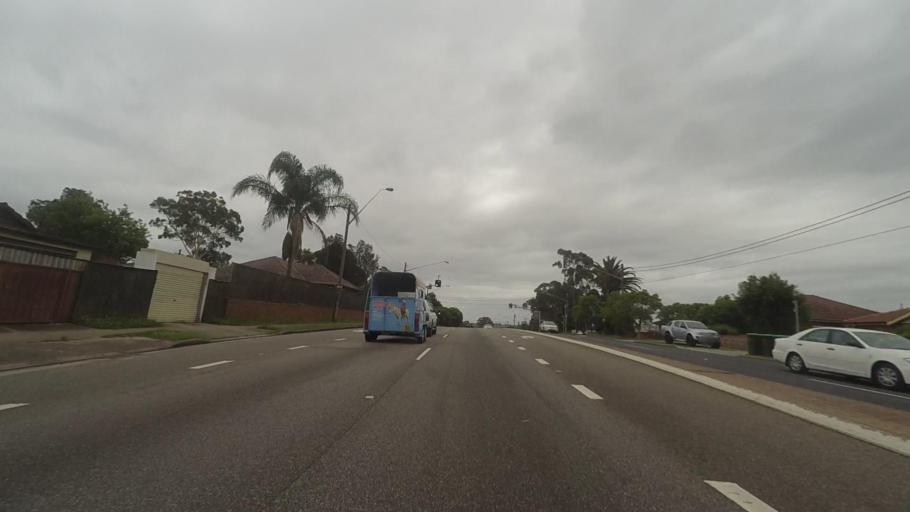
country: AU
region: New South Wales
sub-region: Bankstown
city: Padstow
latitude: -33.9546
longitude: 151.0381
